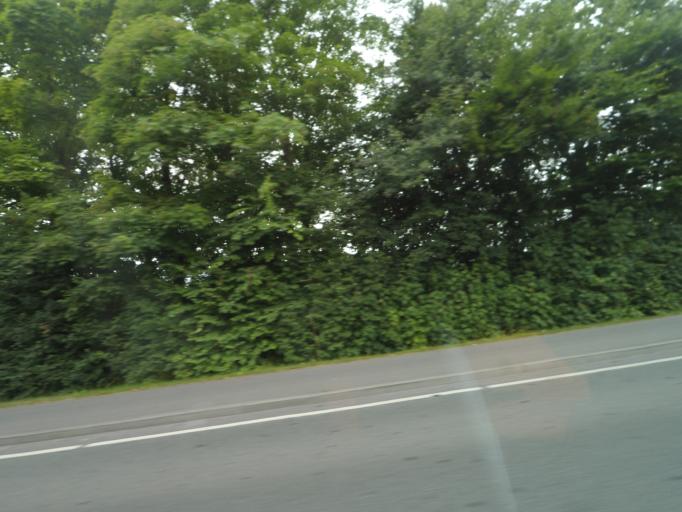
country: DK
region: South Denmark
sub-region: Nordfyns Kommune
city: Otterup
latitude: 55.5093
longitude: 10.3996
